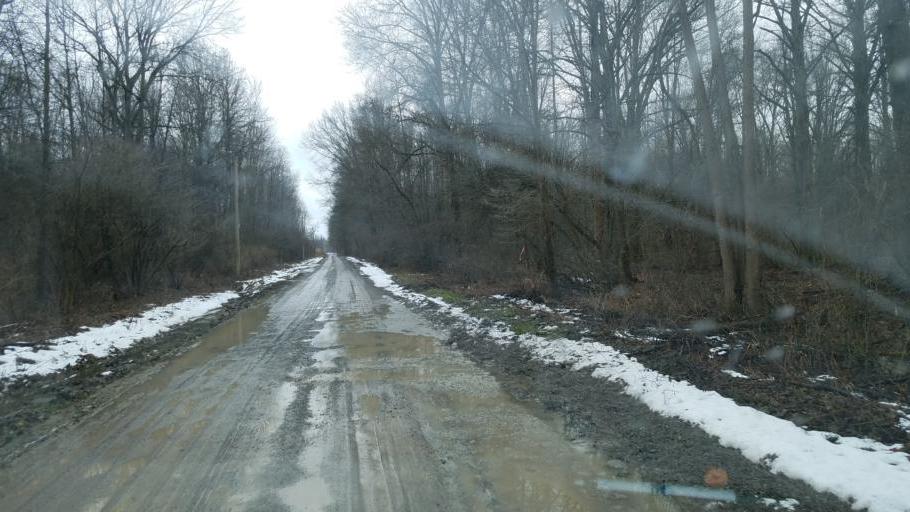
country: US
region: Ohio
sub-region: Ashtabula County
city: Orwell
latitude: 41.4338
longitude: -80.9350
